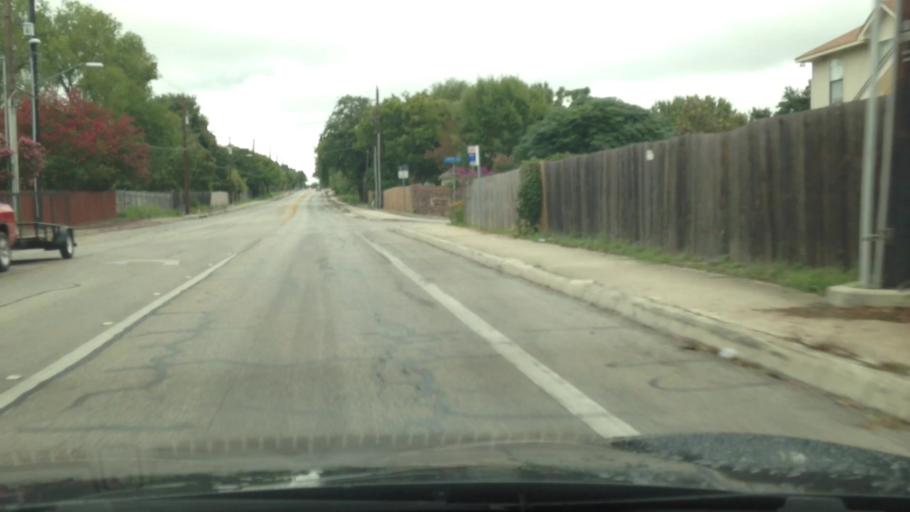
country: US
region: Texas
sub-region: Bexar County
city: Windcrest
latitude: 29.5619
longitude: -98.4000
